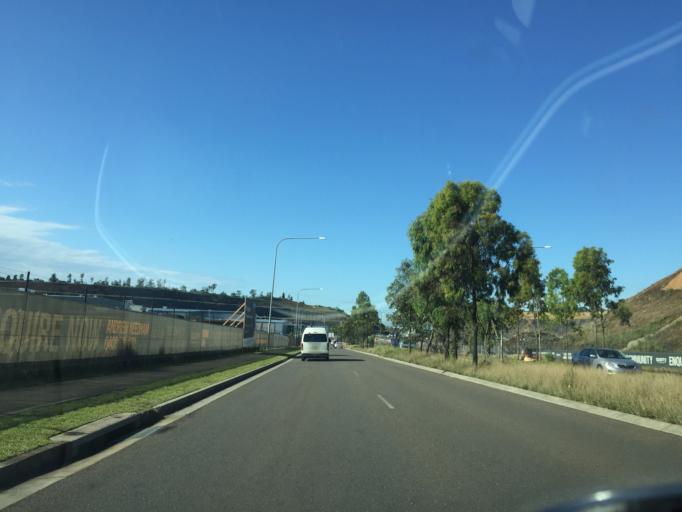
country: AU
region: New South Wales
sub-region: Holroyd
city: Girraween
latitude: -33.8194
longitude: 150.9190
